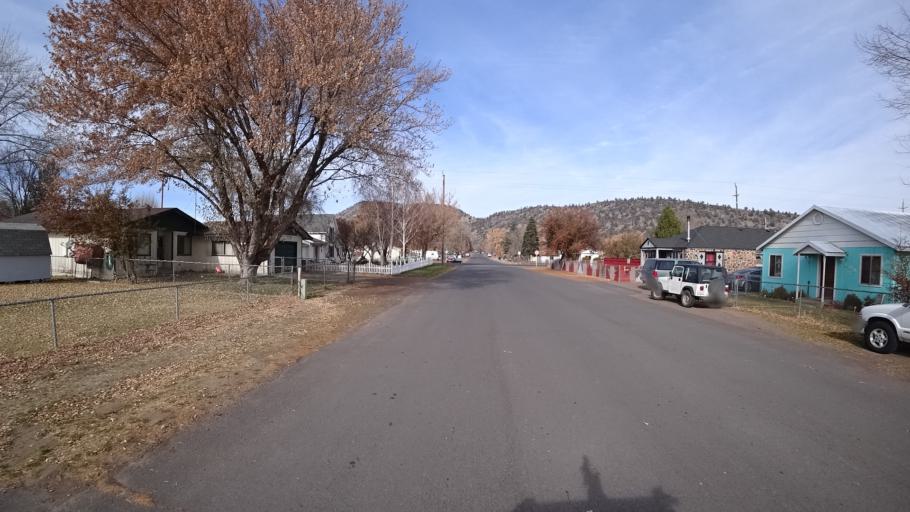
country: US
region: Oregon
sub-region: Klamath County
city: Klamath Falls
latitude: 41.9664
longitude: -121.9207
